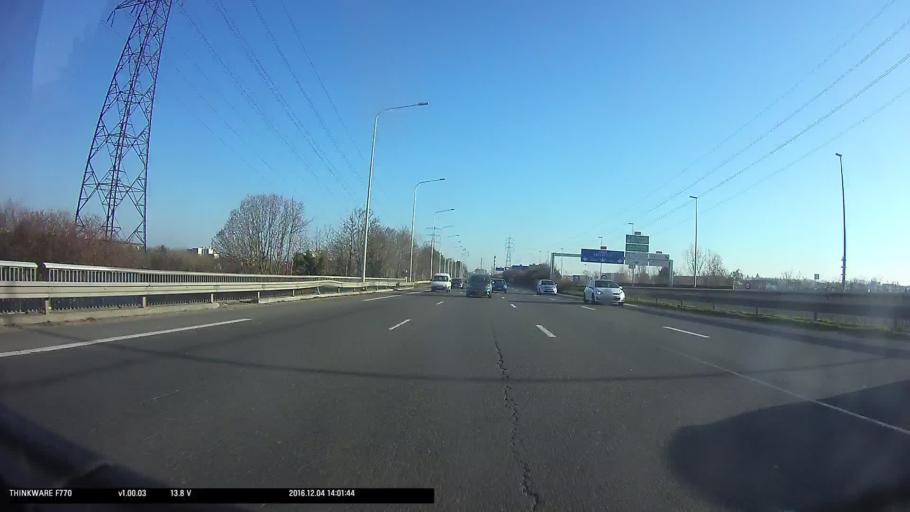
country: FR
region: Ile-de-France
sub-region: Departement du Val-d'Oise
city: Pontoise
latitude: 49.0357
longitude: 2.0977
